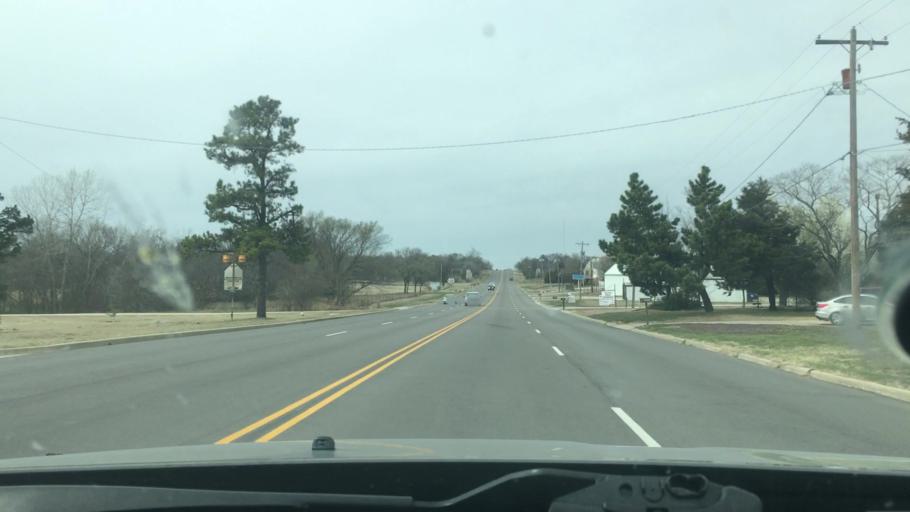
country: US
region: Oklahoma
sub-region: Seminole County
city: Seminole
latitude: 35.2503
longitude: -96.7039
